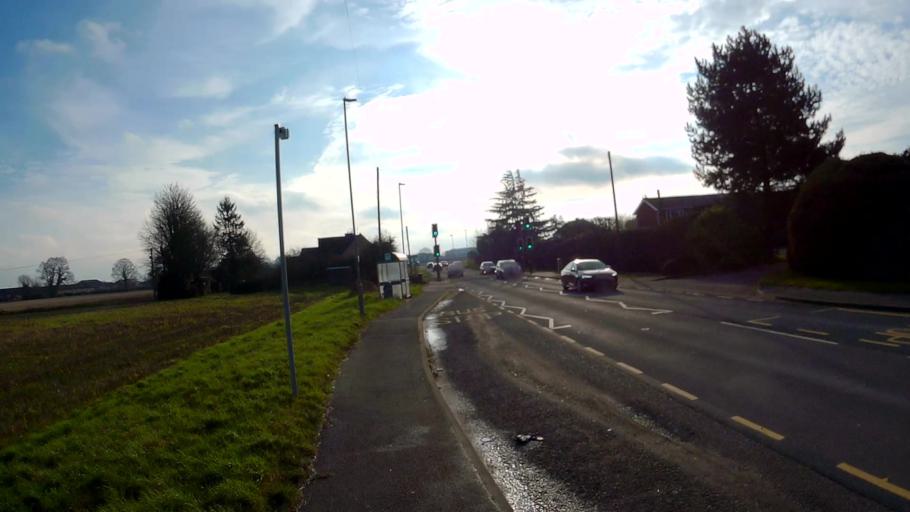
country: GB
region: England
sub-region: Lincolnshire
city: Bourne
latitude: 52.7454
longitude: -0.3689
